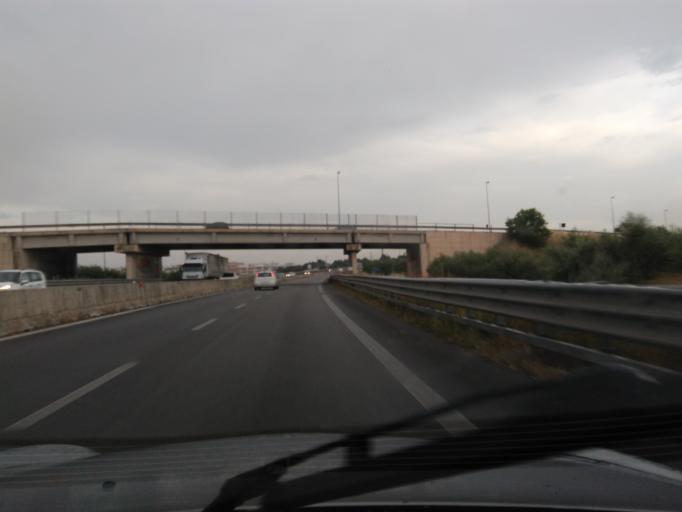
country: IT
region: Apulia
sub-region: Provincia di Bari
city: Molfetta
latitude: 41.1961
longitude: 16.5797
